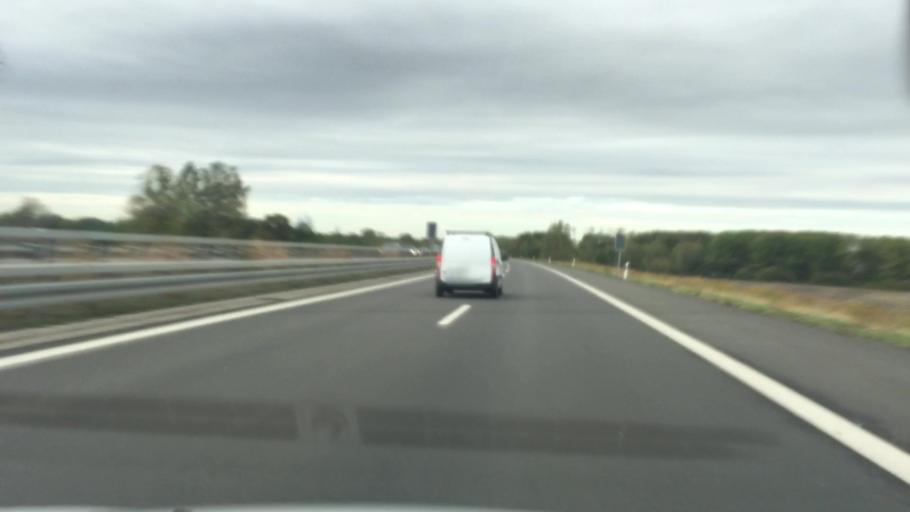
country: DE
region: Saxony
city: Frohburg
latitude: 51.0921
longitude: 12.5315
